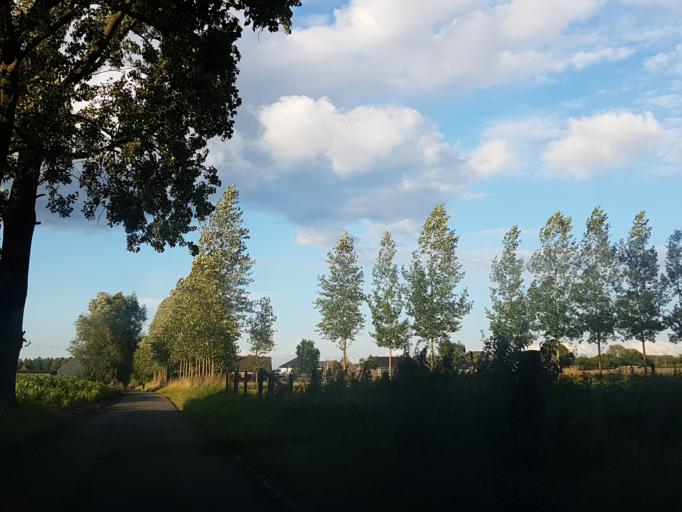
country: BE
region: Flanders
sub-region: Provincie Vlaams-Brabant
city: Opwijk
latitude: 50.9512
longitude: 4.1566
